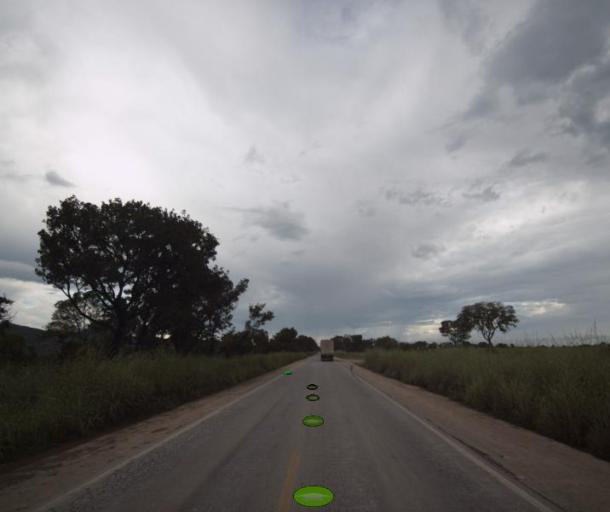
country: BR
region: Goias
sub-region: Porangatu
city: Porangatu
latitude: -13.6059
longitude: -49.0421
